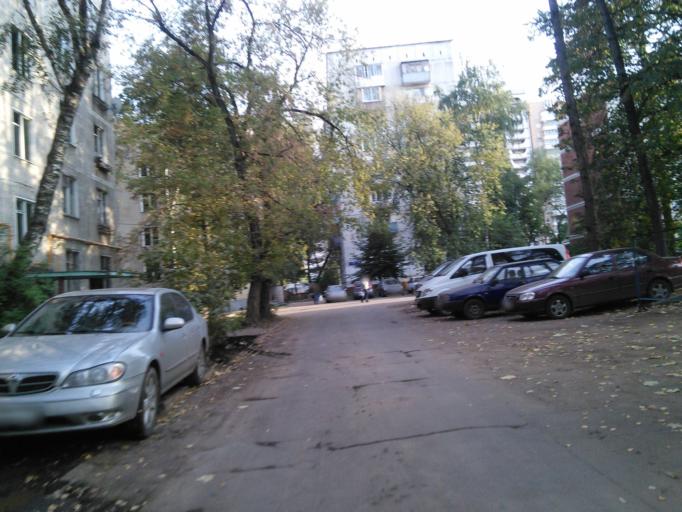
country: RU
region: Moscow
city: Kozeyevo
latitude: 55.8718
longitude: 37.6339
